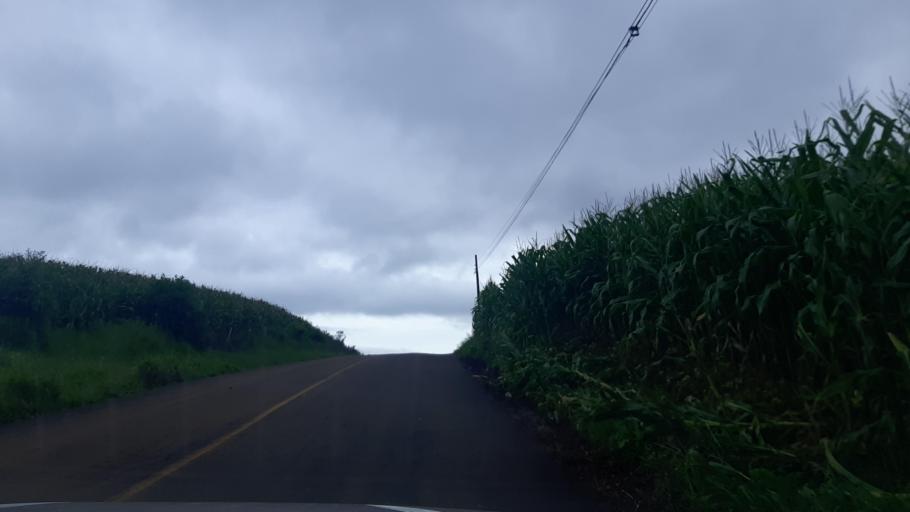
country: BR
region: Parana
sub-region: Ampere
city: Ampere
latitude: -26.0420
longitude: -53.4941
